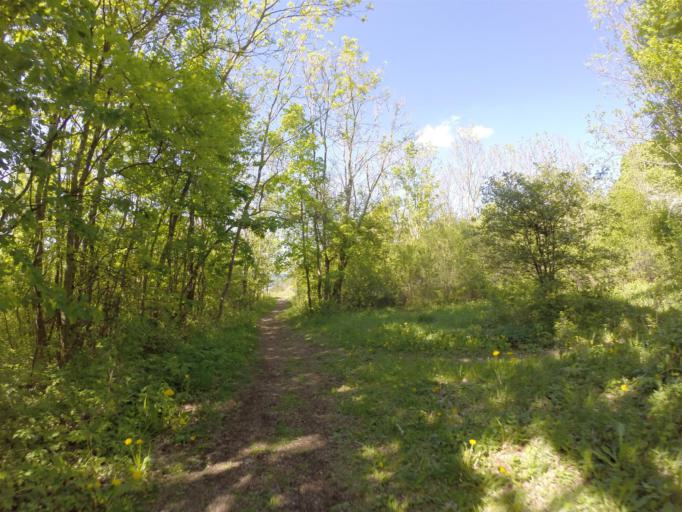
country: DE
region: Thuringia
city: Jena
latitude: 50.9393
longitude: 11.6241
